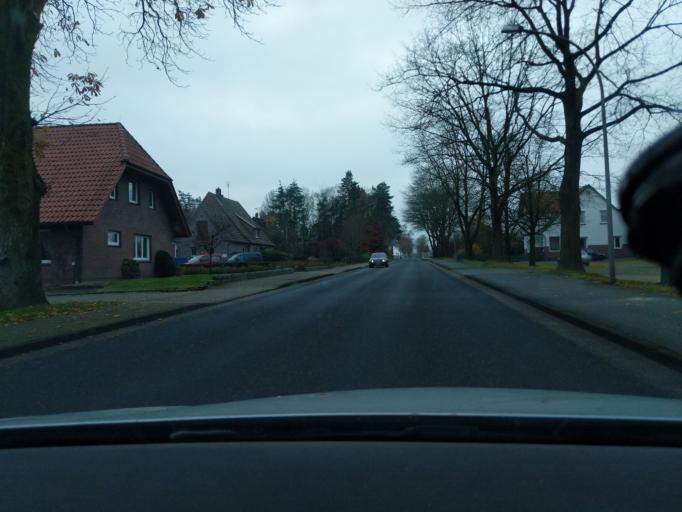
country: DE
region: Lower Saxony
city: Heeslingen
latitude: 53.3450
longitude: 9.3952
